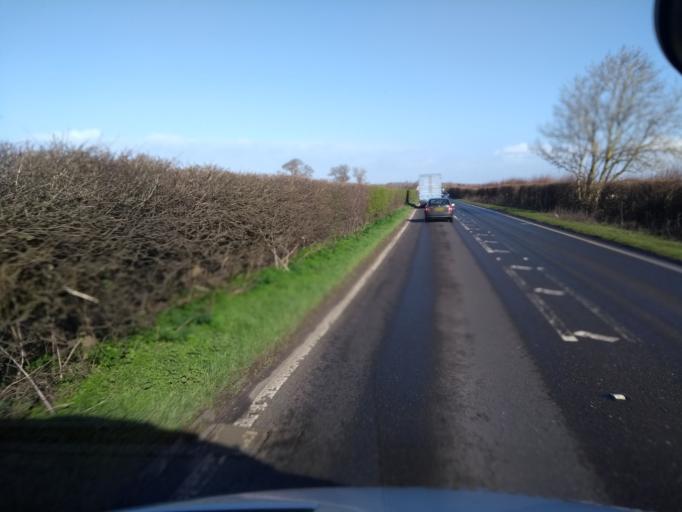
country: GB
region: England
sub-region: Somerset
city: Ilchester
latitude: 50.9895
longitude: -2.6777
